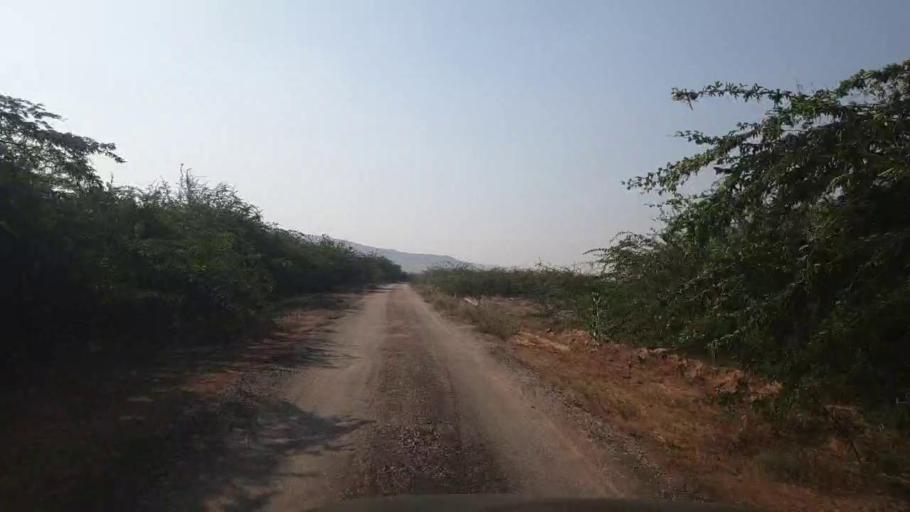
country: PK
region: Sindh
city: Gharo
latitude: 25.0530
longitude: 67.5585
